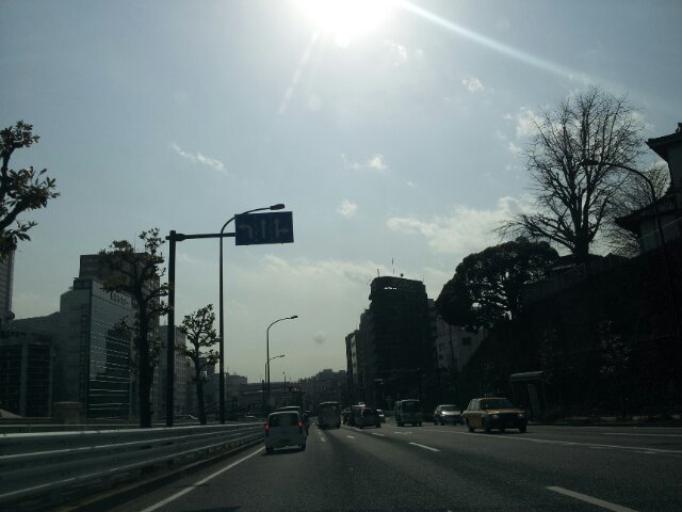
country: JP
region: Kanagawa
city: Yokohama
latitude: 35.4720
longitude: 139.6273
